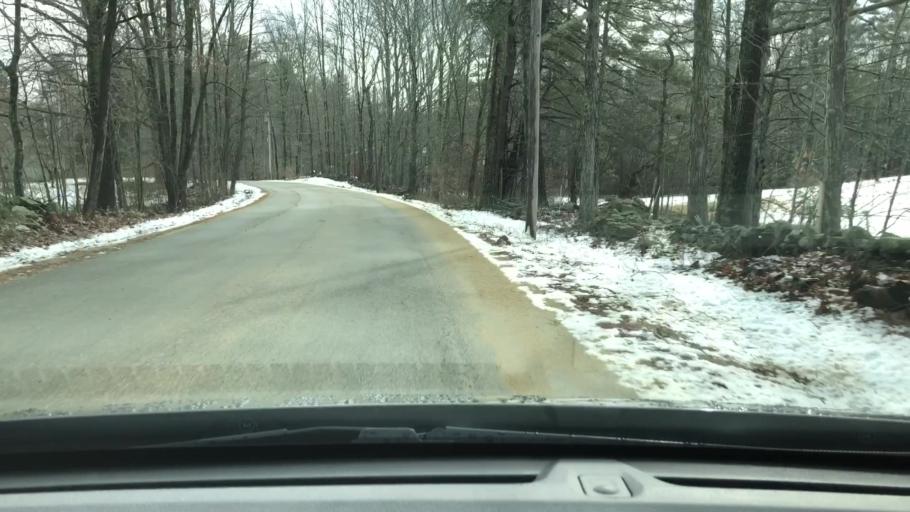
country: US
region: New Hampshire
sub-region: Strafford County
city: Madbury
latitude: 43.1835
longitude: -70.9735
